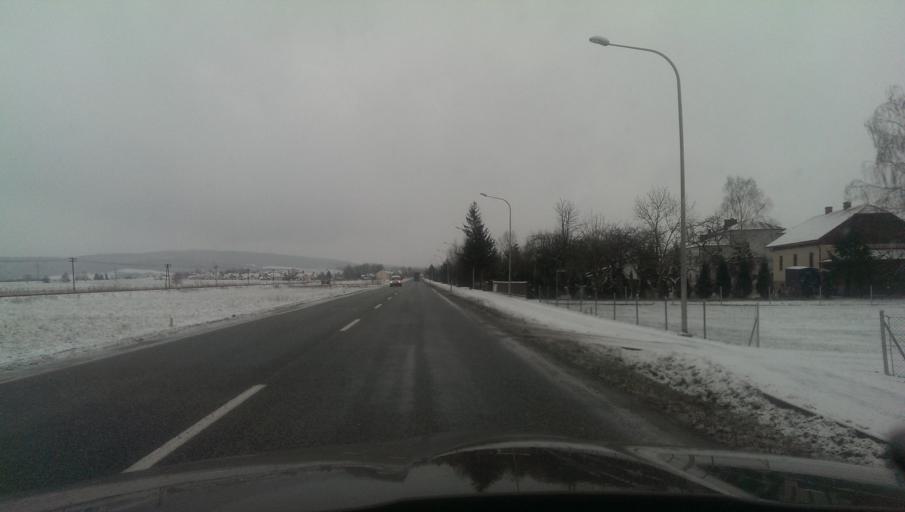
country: PL
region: Subcarpathian Voivodeship
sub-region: Powiat sanocki
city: Dlugie
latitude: 49.5807
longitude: 22.0321
